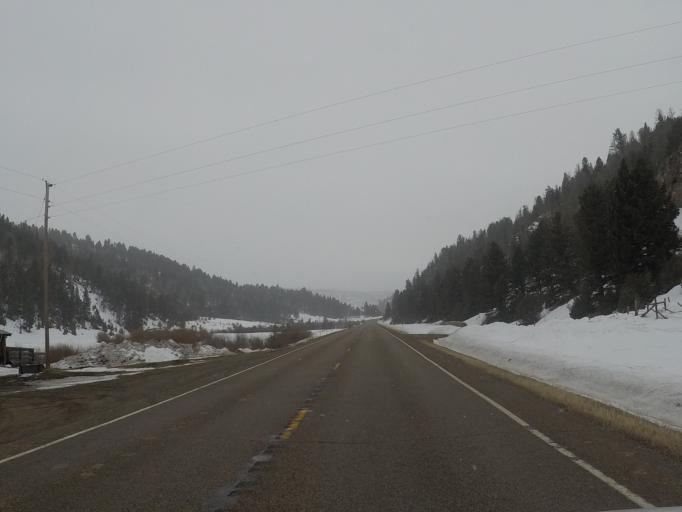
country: US
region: Montana
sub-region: Meagher County
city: White Sulphur Springs
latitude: 46.6863
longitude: -110.8737
